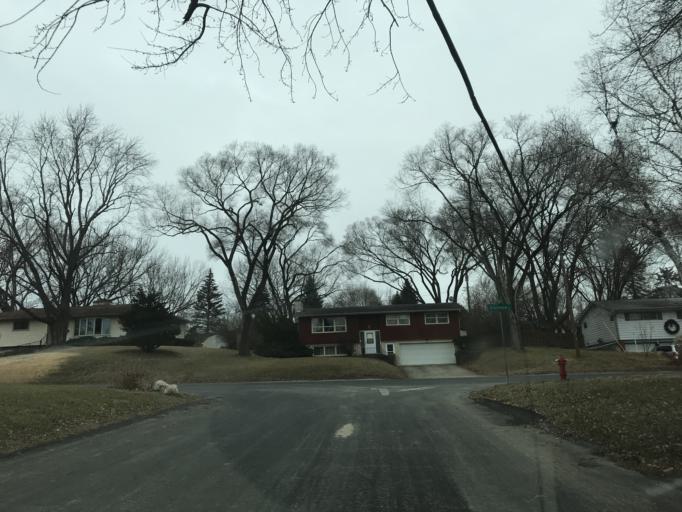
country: US
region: Wisconsin
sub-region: Dane County
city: Monona
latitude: 43.0572
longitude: -89.3171
